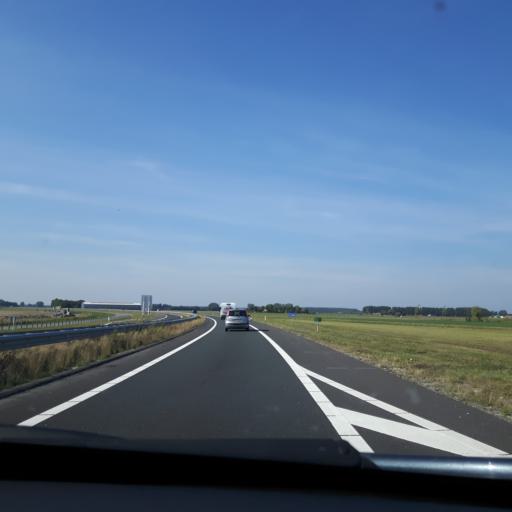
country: NL
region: Zeeland
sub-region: Gemeente Borsele
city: Borssele
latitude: 51.3252
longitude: 3.6793
